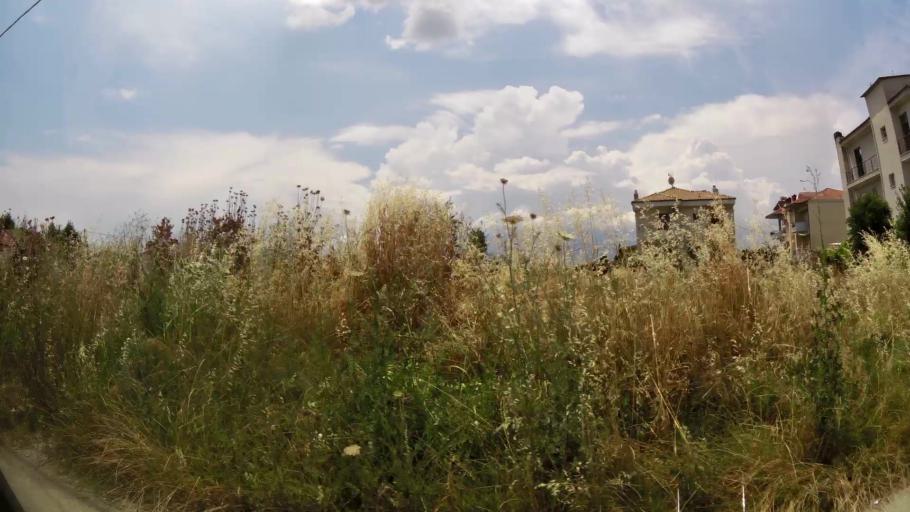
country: GR
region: Central Macedonia
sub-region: Nomos Pierias
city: Peristasi
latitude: 40.2714
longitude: 22.5479
